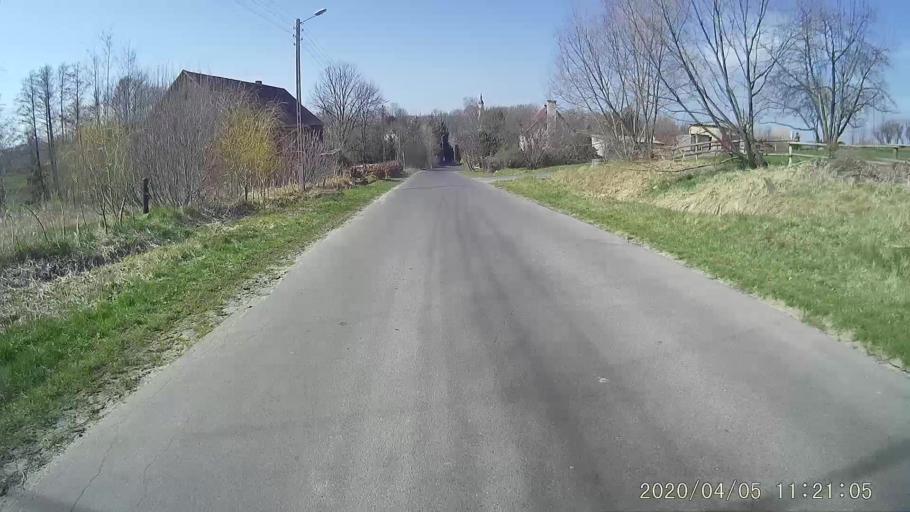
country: PL
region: Lower Silesian Voivodeship
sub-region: Powiat zgorzelecki
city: Sulikow
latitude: 51.0539
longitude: 15.1164
